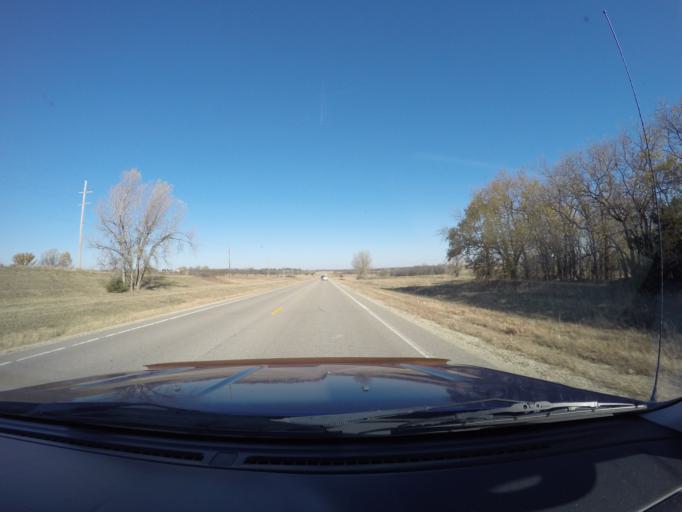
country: US
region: Kansas
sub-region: Riley County
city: Ogden
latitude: 39.3527
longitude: -96.7565
